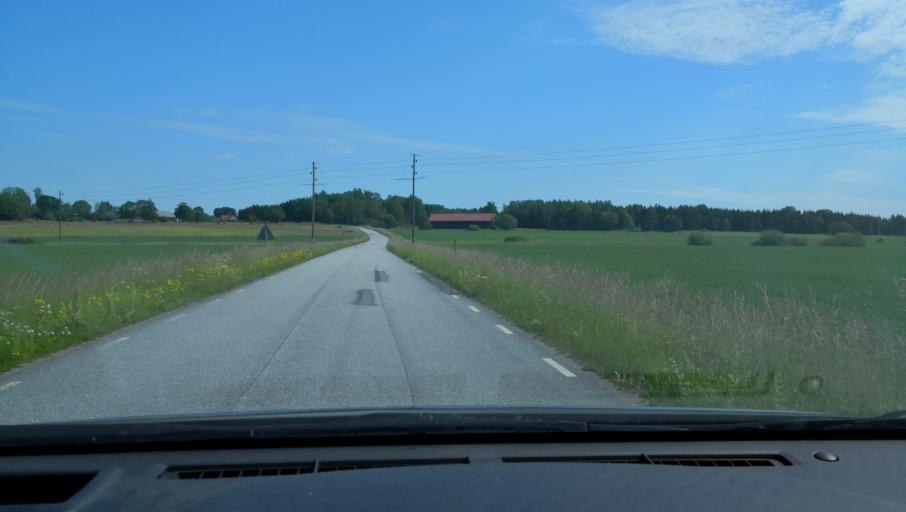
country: SE
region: Uppsala
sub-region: Enkopings Kommun
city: Enkoping
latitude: 59.6956
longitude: 17.1047
